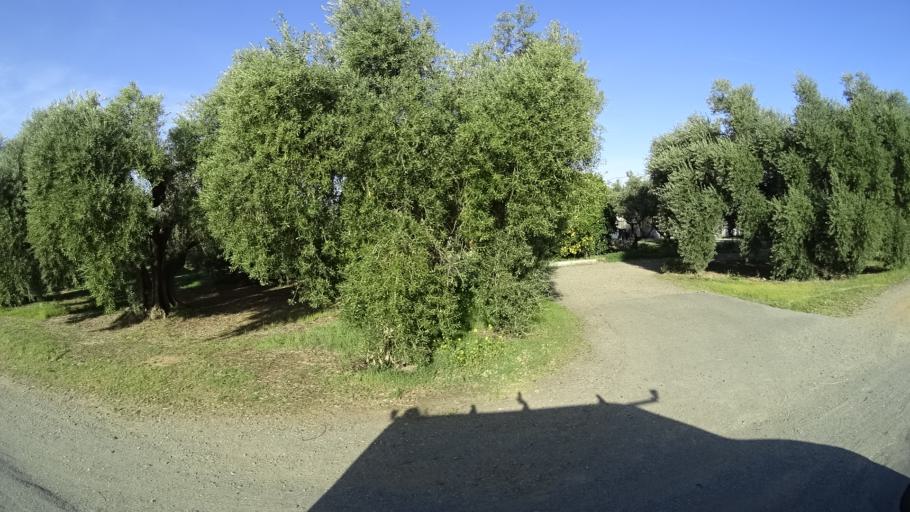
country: US
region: California
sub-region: Glenn County
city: Orland
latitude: 39.7305
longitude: -122.2345
